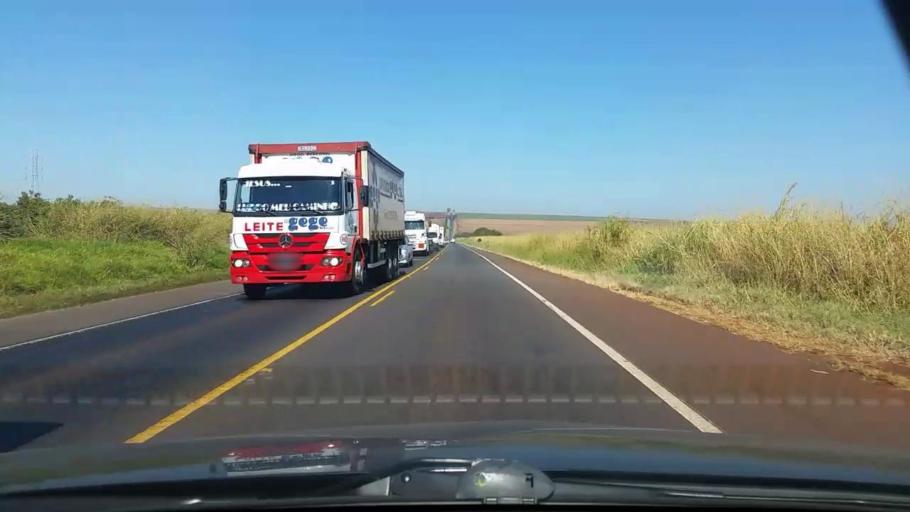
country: BR
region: Sao Paulo
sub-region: Jau
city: Jau
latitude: -22.3584
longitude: -48.5724
